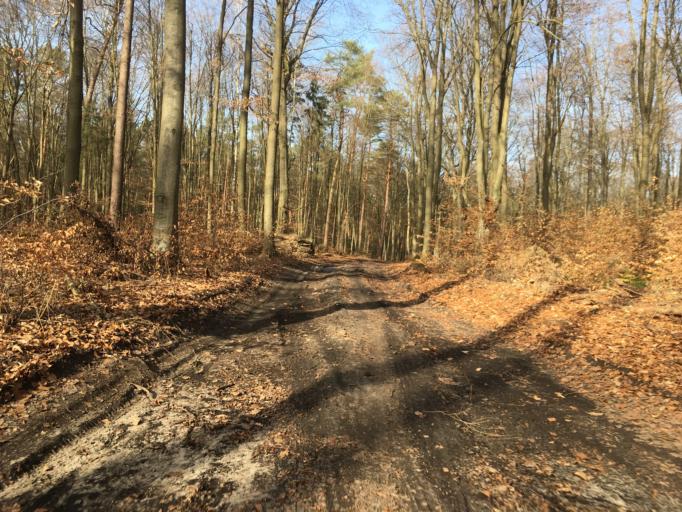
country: DE
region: Brandenburg
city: Wandlitz
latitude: 52.7218
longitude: 13.5236
